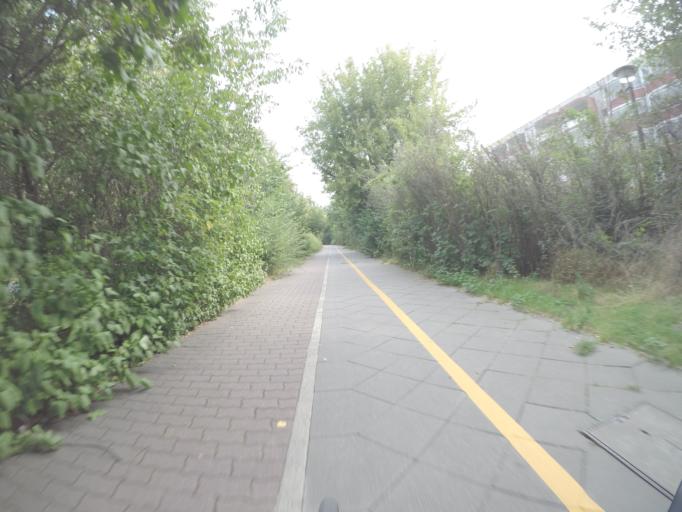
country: DE
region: Berlin
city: Buch
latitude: 52.6267
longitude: 13.4967
